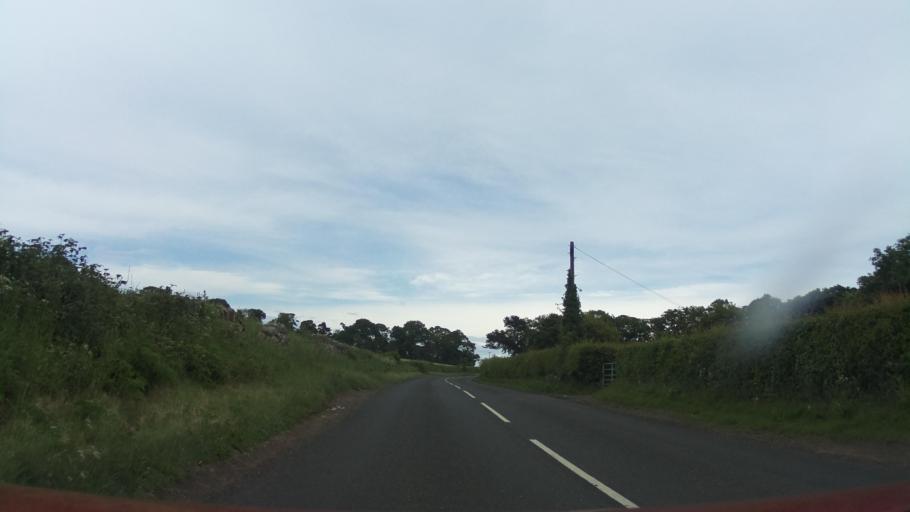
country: GB
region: Scotland
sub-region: East Lothian
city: Prestonpans
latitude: 55.9122
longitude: -3.0052
